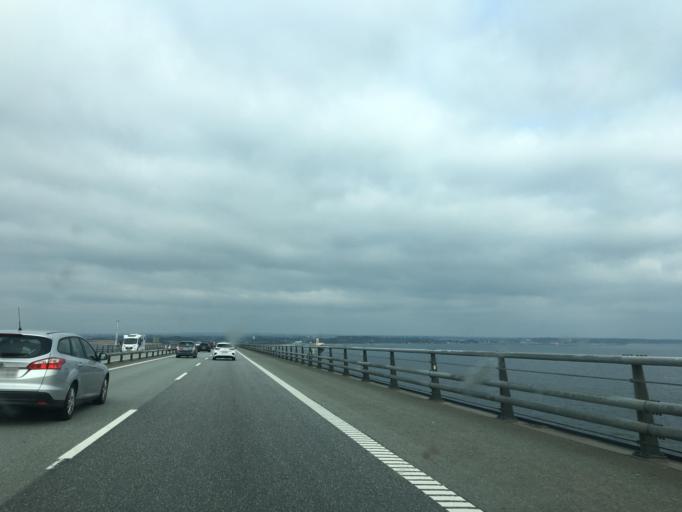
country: DK
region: Zealand
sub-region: Slagelse Kommune
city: Korsor
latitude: 55.3453
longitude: 11.0560
